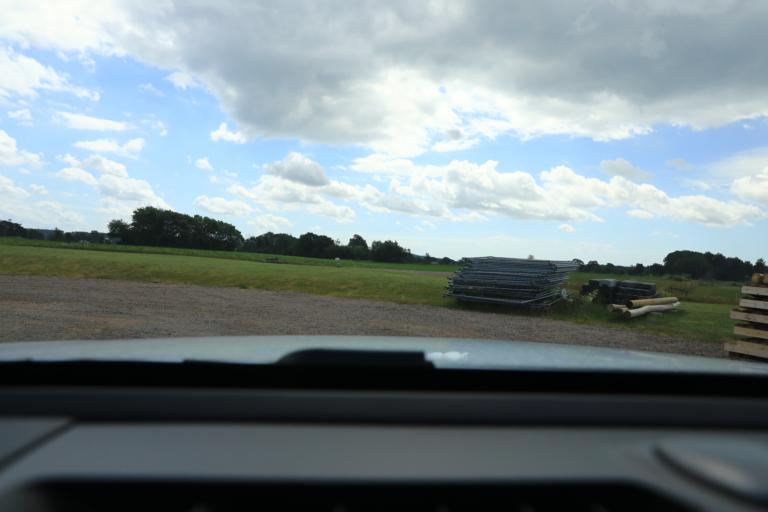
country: SE
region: Halland
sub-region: Varbergs Kommun
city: Tvaaker
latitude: 57.1127
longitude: 12.4056
